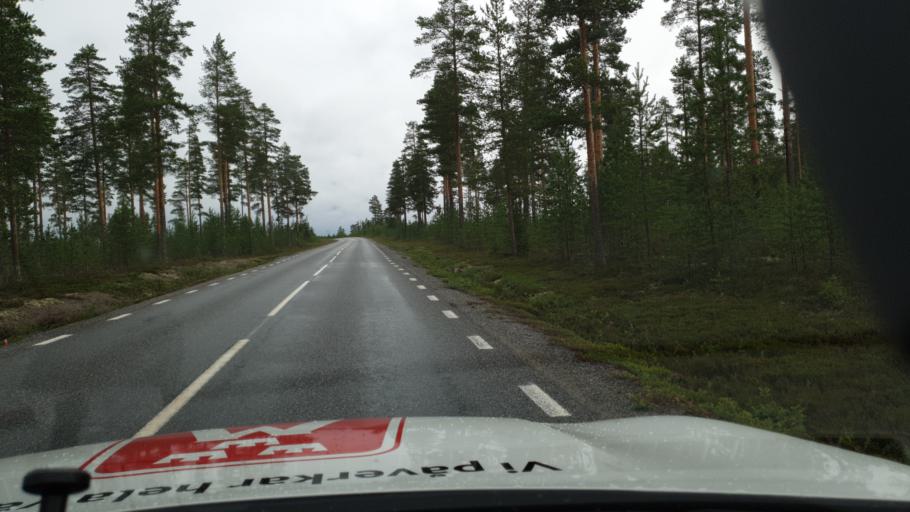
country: SE
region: Vaesterbotten
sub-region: Umea Kommun
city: Saevar
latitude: 63.9672
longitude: 20.5073
